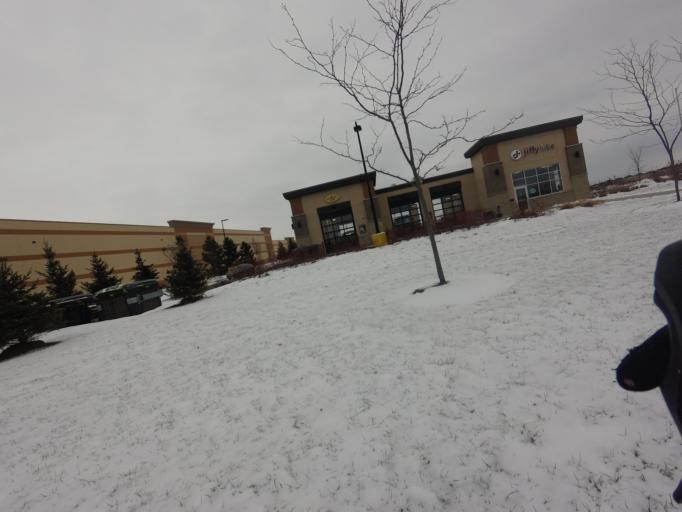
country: CA
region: Ontario
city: Bells Corners
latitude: 45.2760
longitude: -75.8724
